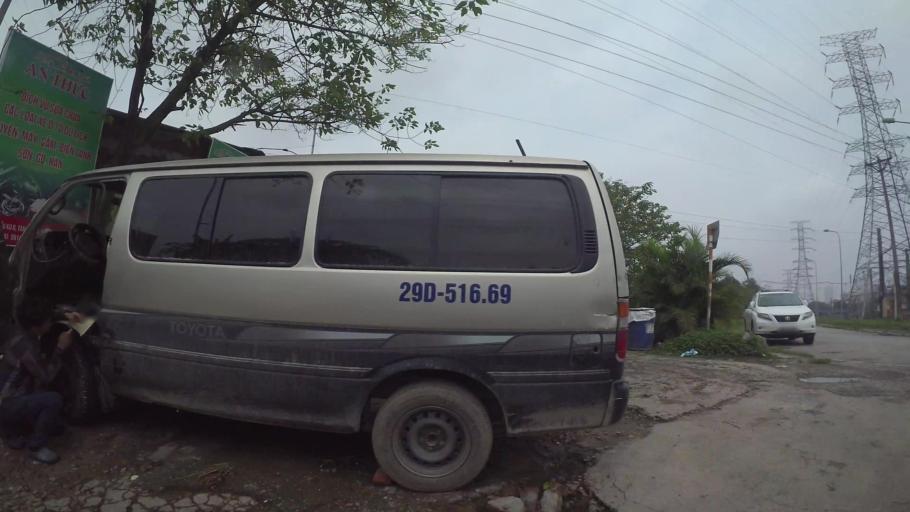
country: VN
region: Ha Noi
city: Van Dien
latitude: 20.9760
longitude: 105.8652
